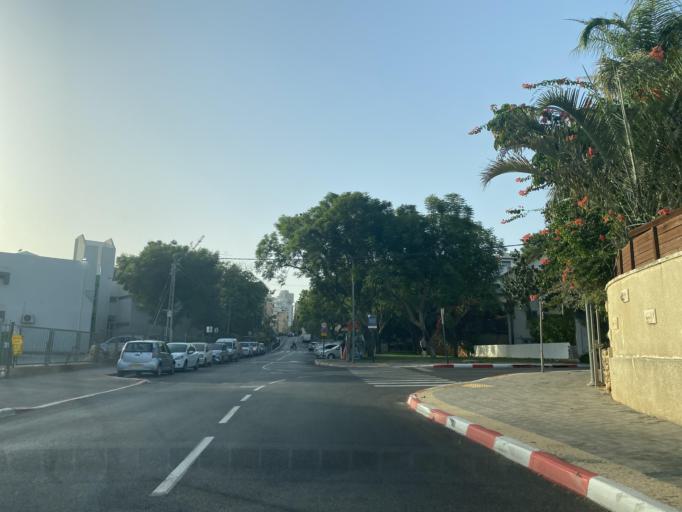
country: IL
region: Central District
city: Hod HaSharon
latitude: 32.1563
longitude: 34.9022
